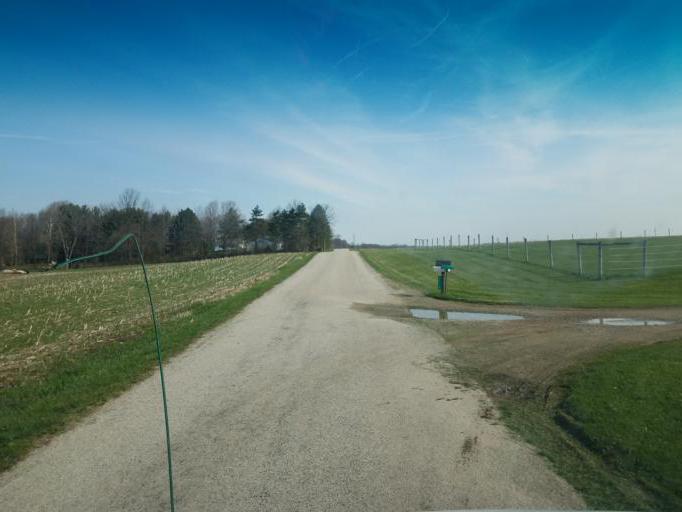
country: US
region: Ohio
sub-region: Richland County
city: Shelby
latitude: 40.8845
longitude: -82.5714
